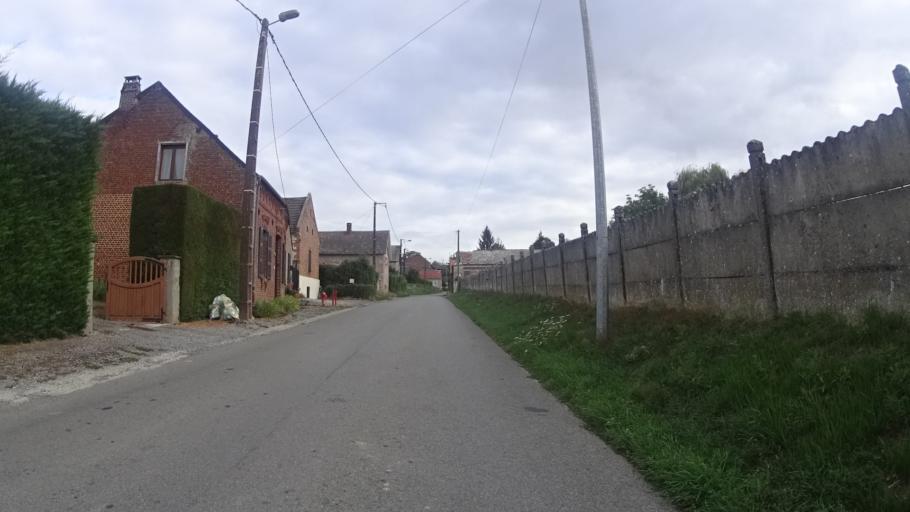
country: FR
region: Picardie
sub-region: Departement de l'Aisne
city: Guise
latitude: 49.9353
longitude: 3.5825
